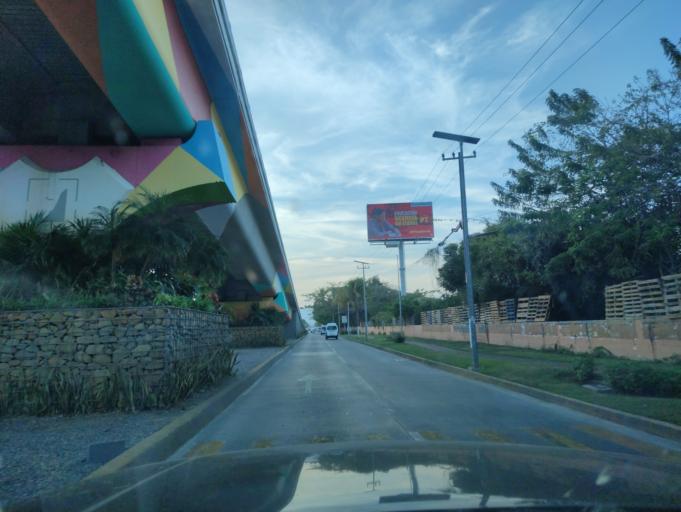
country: MX
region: Guerrero
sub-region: Acapulco de Juarez
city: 10 de Abril
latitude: 16.7726
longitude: -99.7738
